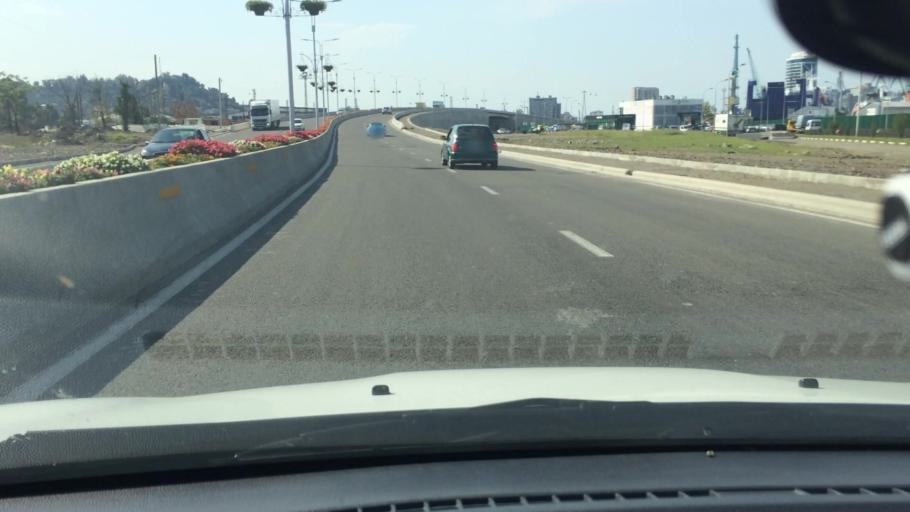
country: GE
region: Ajaria
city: Batumi
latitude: 41.6484
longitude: 41.6620
